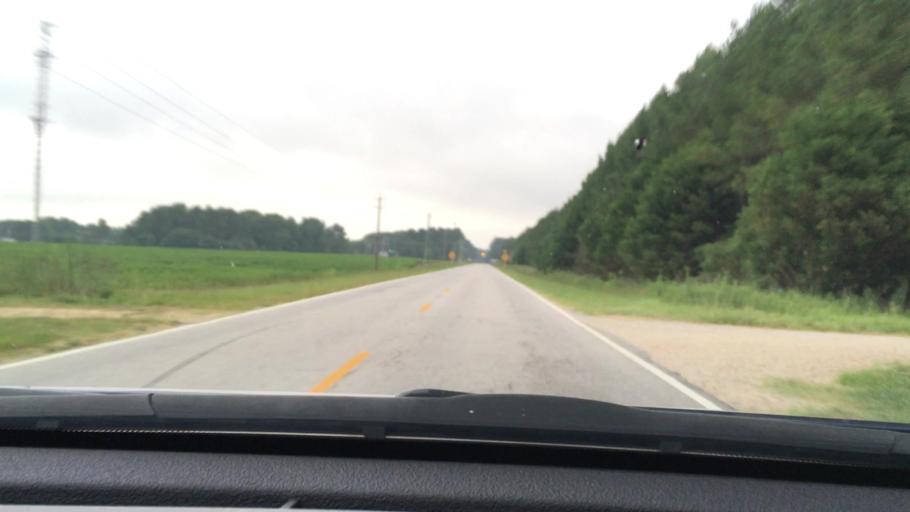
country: US
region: South Carolina
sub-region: Lee County
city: Bishopville
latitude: 34.1162
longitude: -80.1484
